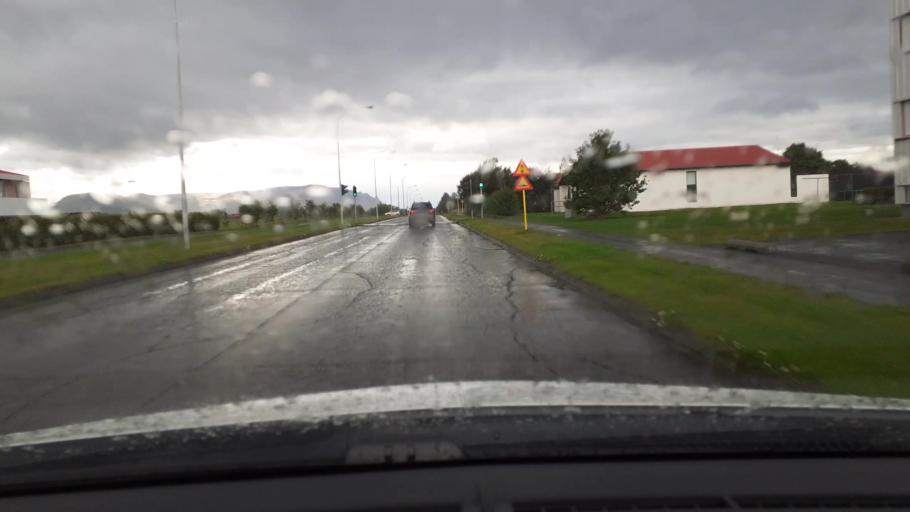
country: IS
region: West
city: Akranes
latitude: 64.3203
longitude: -22.0525
